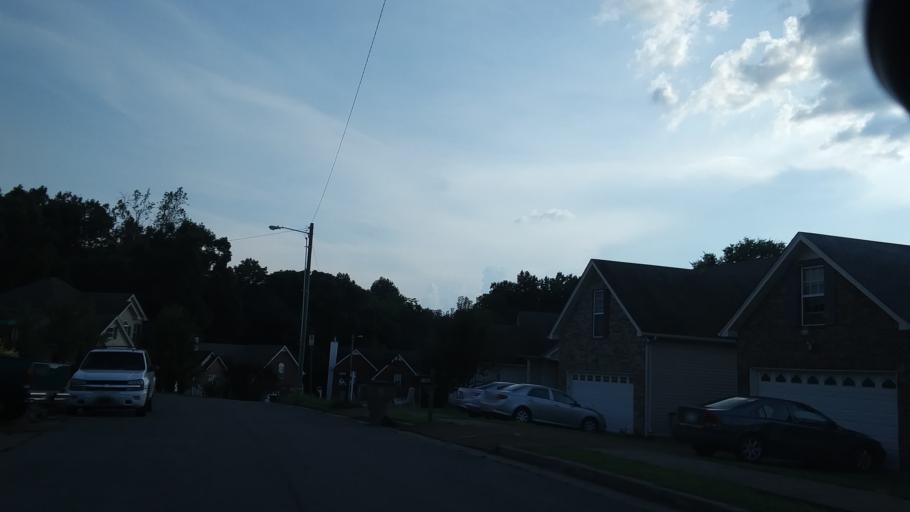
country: US
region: Tennessee
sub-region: Rutherford County
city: La Vergne
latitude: 36.0893
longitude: -86.6576
